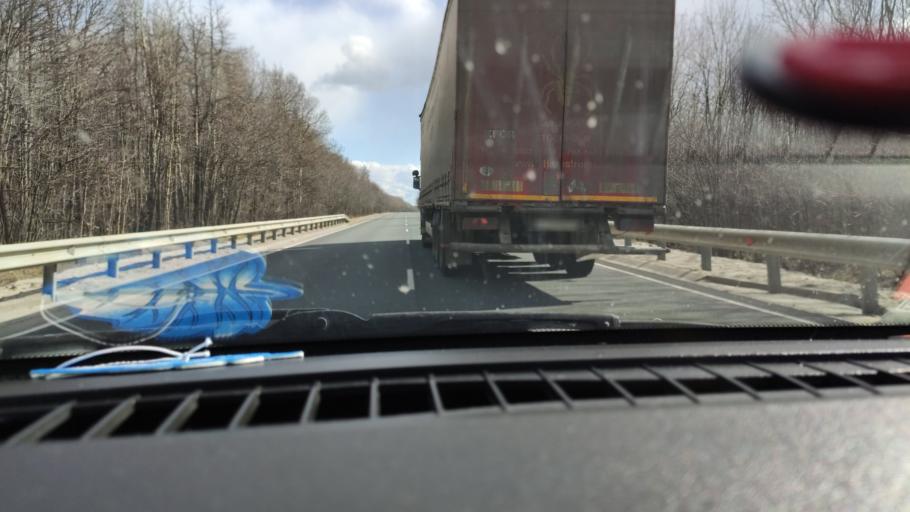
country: RU
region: Saratov
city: Khvalynsk
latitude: 52.4655
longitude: 48.0174
